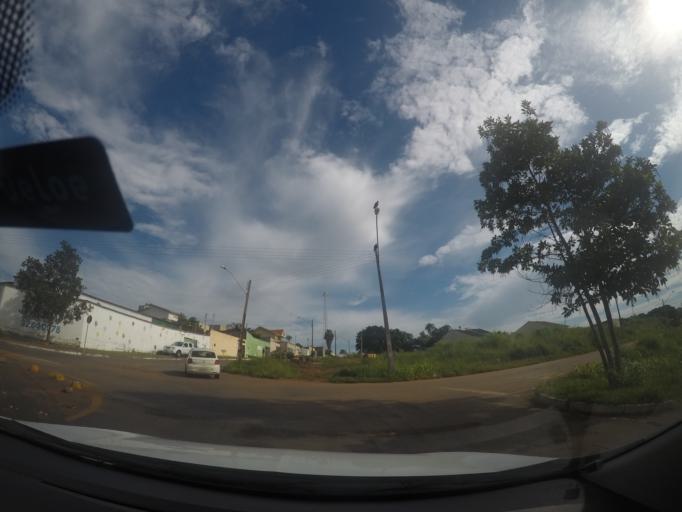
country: BR
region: Goias
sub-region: Goiania
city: Goiania
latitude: -16.6755
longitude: -49.2026
